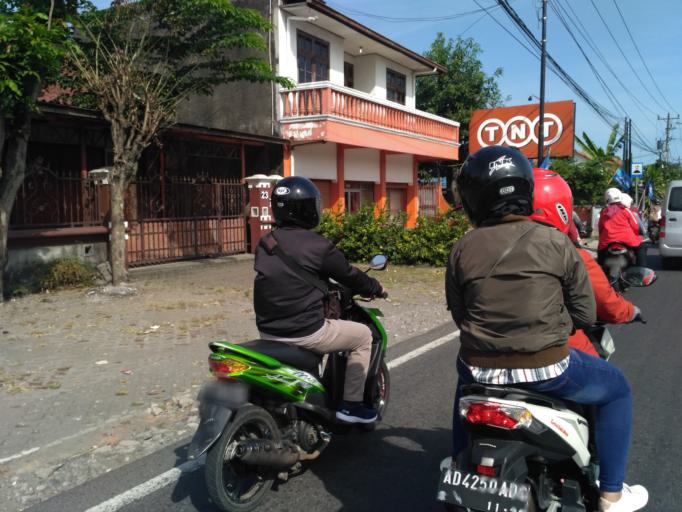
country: ID
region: Daerah Istimewa Yogyakarta
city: Depok
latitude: -7.7694
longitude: 110.4313
